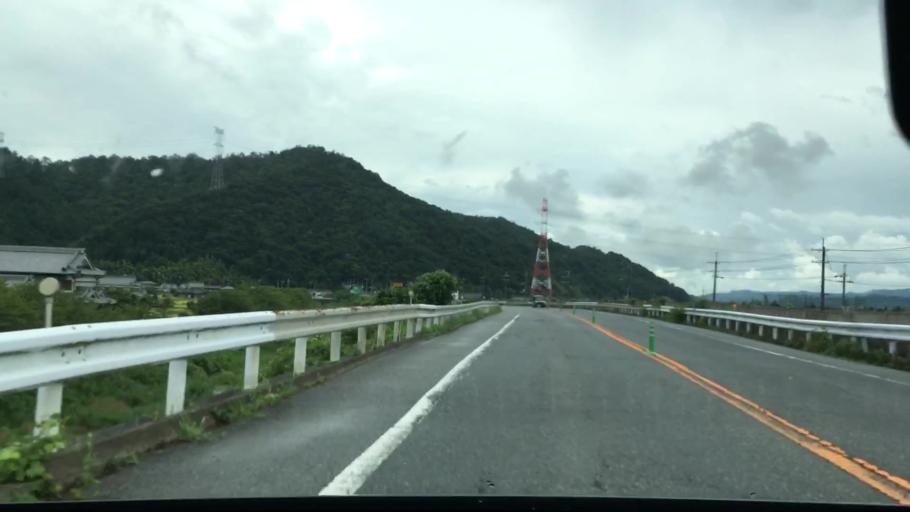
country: JP
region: Hyogo
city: Himeji
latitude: 34.9778
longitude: 134.7687
